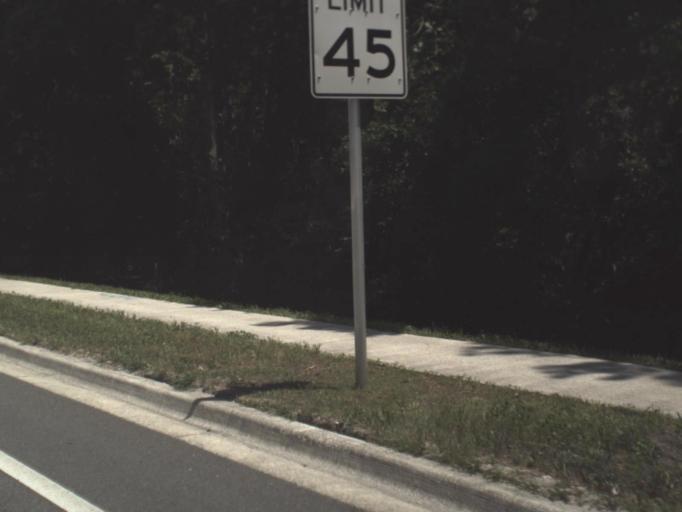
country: US
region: Florida
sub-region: Duval County
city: Neptune Beach
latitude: 30.2872
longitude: -81.4934
